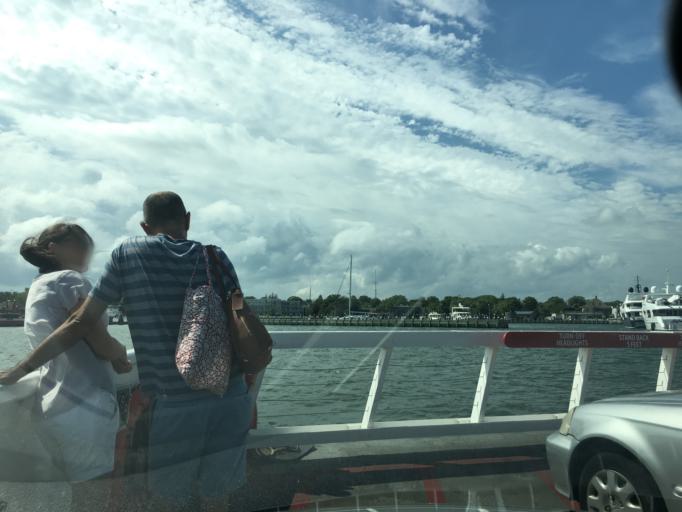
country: US
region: New York
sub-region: Suffolk County
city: Greenport
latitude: 41.0989
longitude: -72.3591
